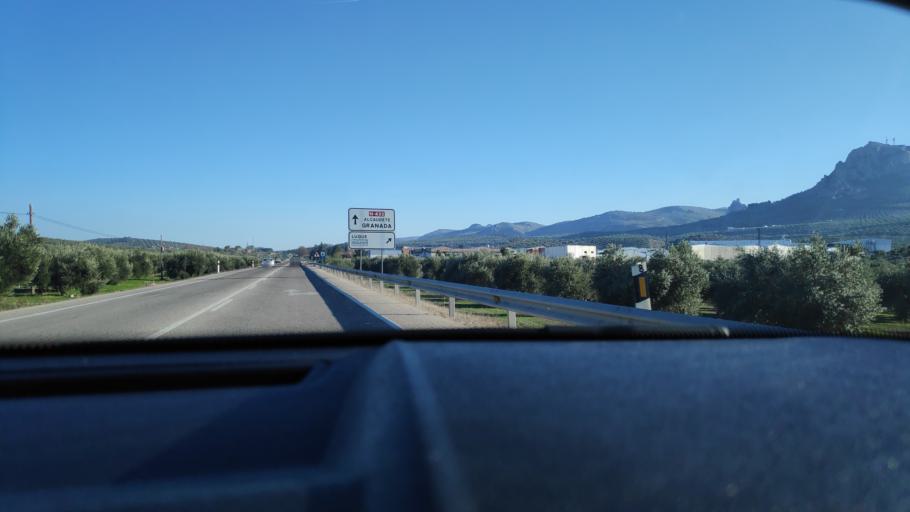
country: ES
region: Andalusia
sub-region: Province of Cordoba
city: Luque
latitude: 37.5833
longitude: -4.2881
